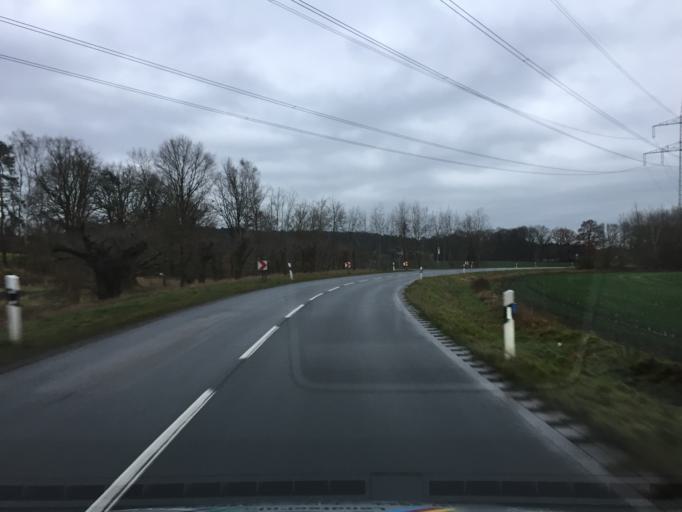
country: DE
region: Lower Saxony
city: Pennigsehl
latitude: 52.6221
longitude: 8.9968
